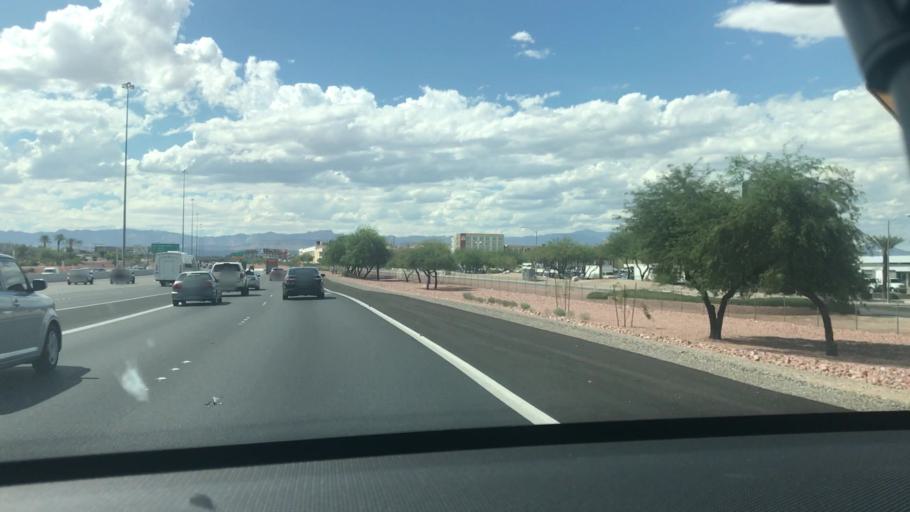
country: US
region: Nevada
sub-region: Clark County
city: Paradise
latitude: 36.0642
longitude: -115.1539
